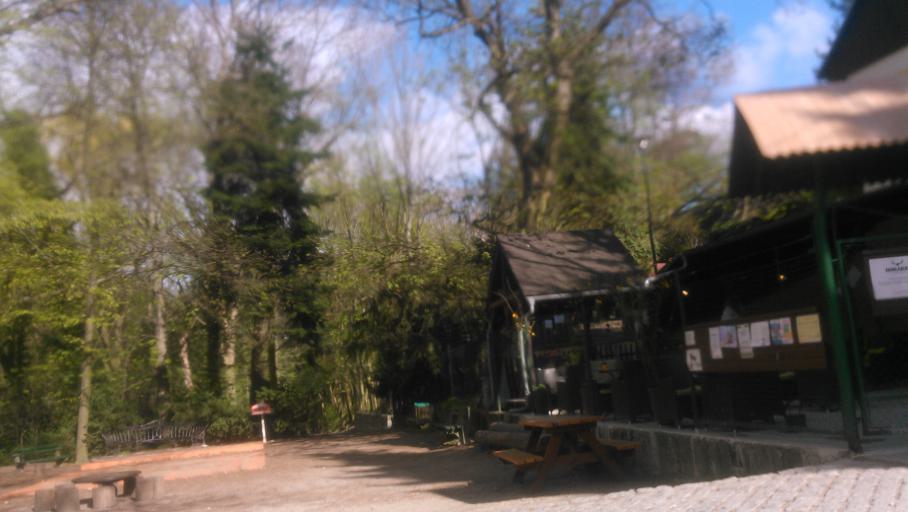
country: SK
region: Bratislavsky
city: Bratislava
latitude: 48.1567
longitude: 17.0948
